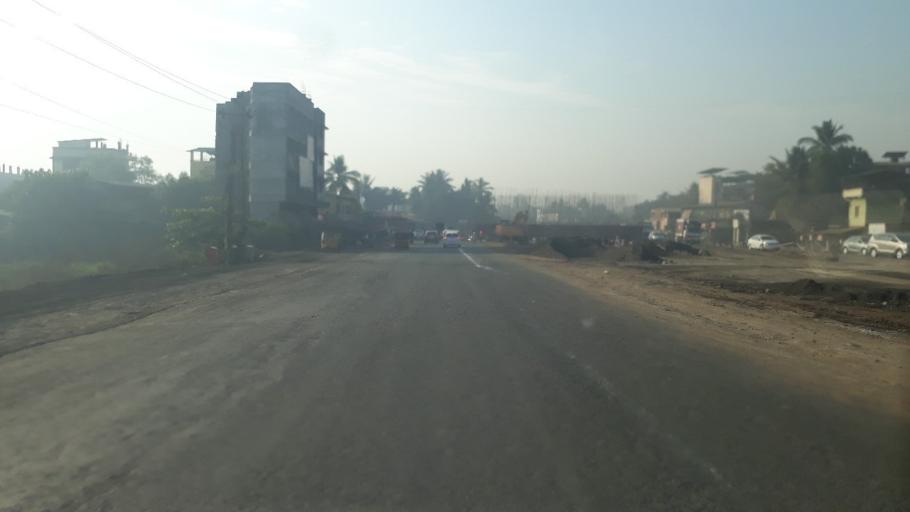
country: IN
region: Maharashtra
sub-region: Raigarh
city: Kalundri
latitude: 18.9606
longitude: 73.1312
